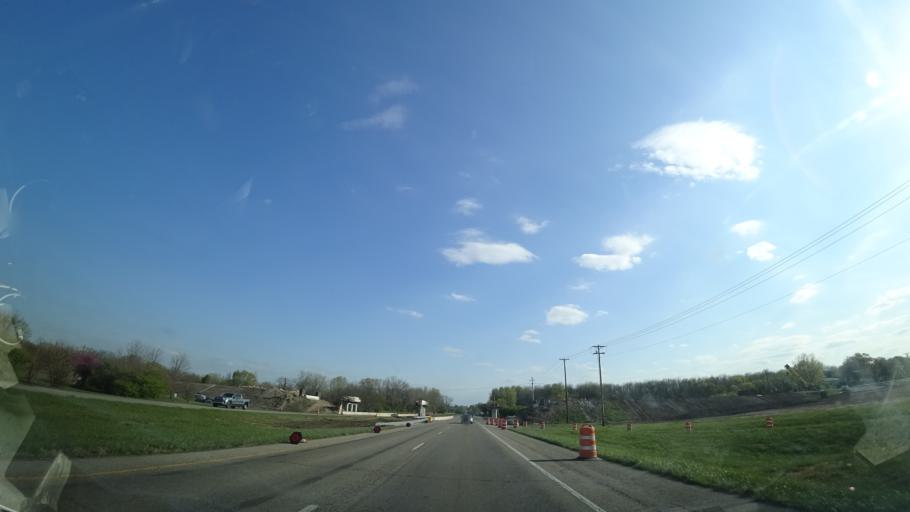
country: US
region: Ohio
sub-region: Greene County
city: Wright-Patterson AFB
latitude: 39.8449
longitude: -84.0590
